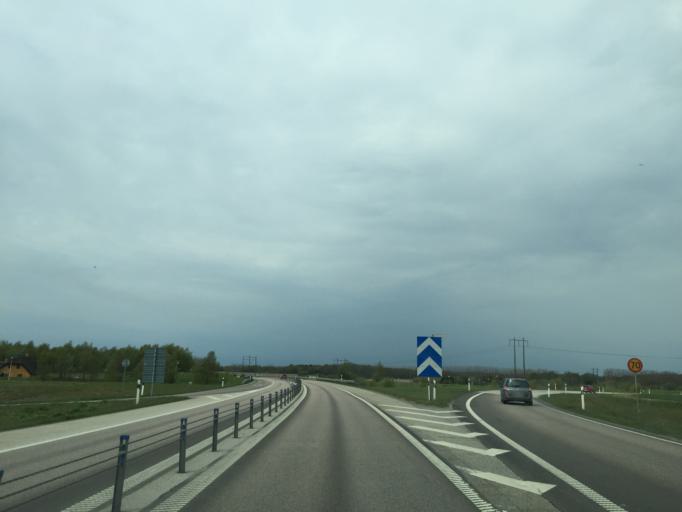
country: SE
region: Skane
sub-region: Helsingborg
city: Odakra
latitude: 56.0925
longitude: 12.7014
